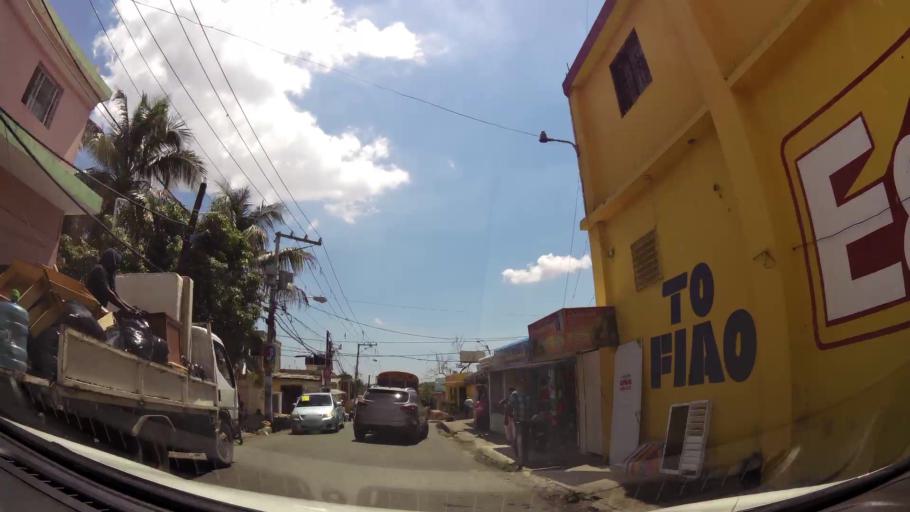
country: DO
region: Santo Domingo
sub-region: Santo Domingo
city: Santo Domingo Este
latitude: 18.5406
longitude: -69.8631
